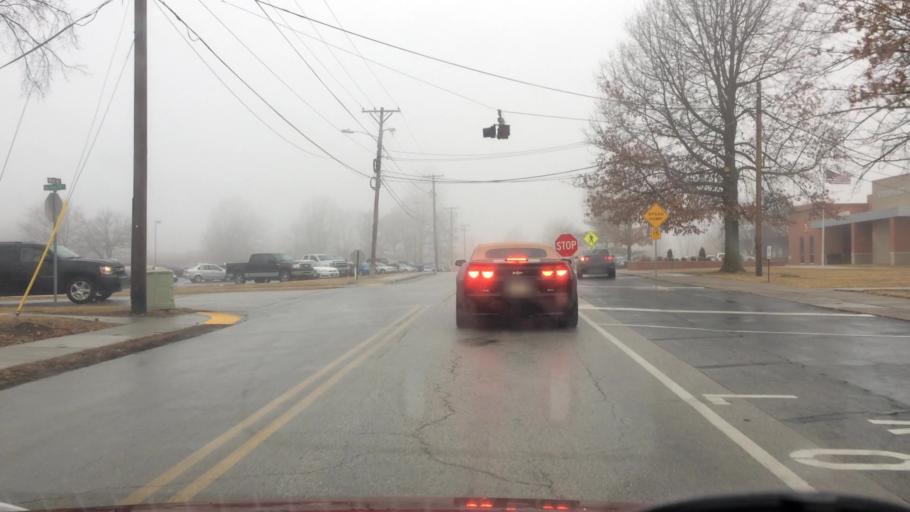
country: US
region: Missouri
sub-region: Greene County
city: Strafford
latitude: 37.2707
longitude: -93.1186
